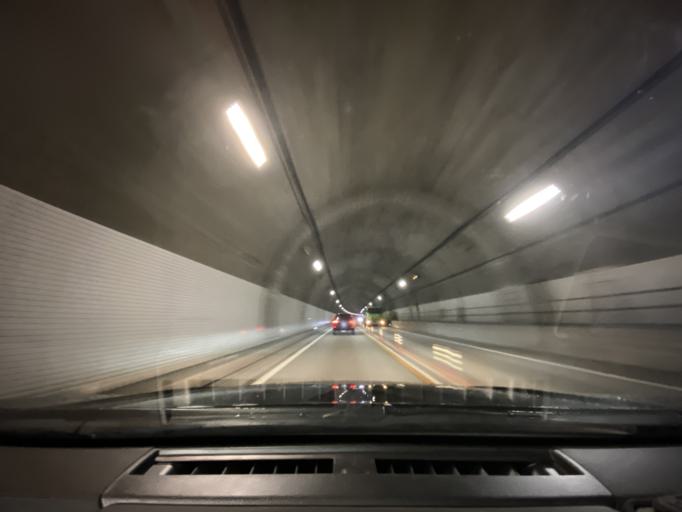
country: JP
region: Hokkaido
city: Iwamizawa
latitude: 42.9357
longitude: 142.0900
